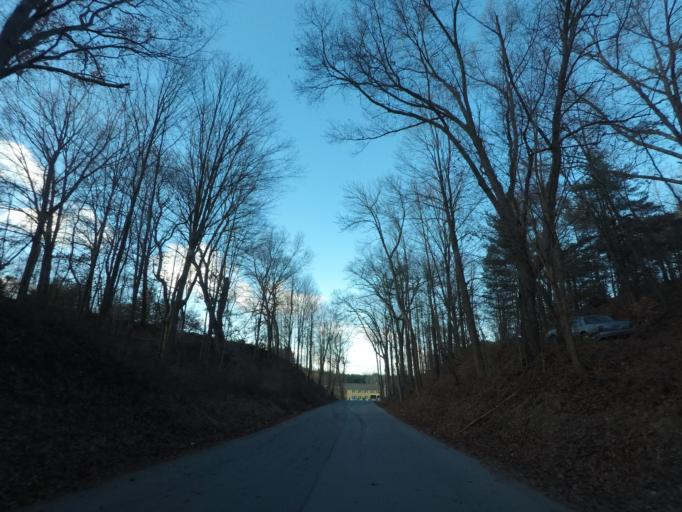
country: US
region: New York
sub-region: Saratoga County
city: Country Knolls
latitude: 42.8884
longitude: -73.7701
